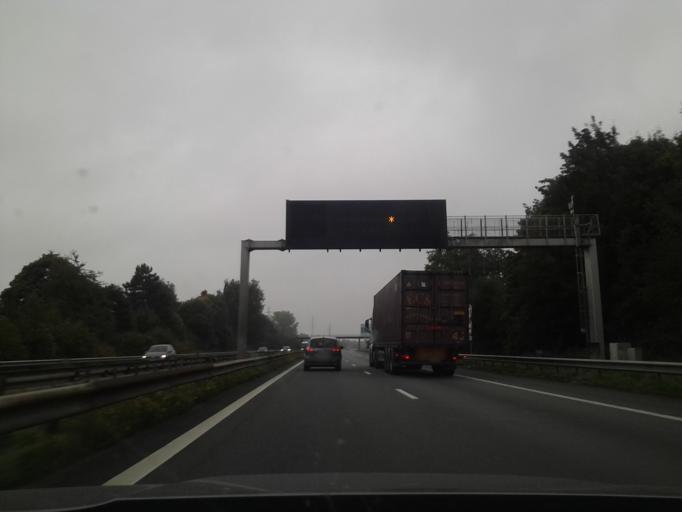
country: FR
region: Nord-Pas-de-Calais
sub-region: Departement du Nord
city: Lieu-Saint-Amand
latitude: 50.2667
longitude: 3.3323
